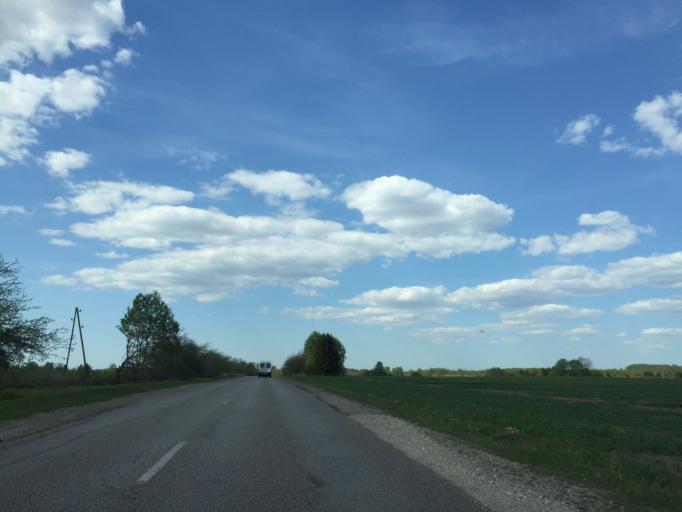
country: LV
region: Limbazu Rajons
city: Limbazi
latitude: 57.4581
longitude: 24.7209
